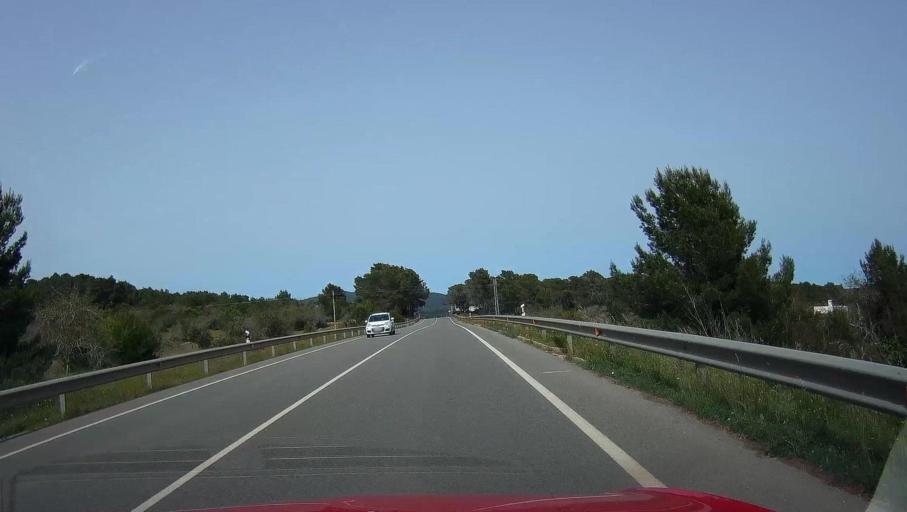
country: ES
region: Balearic Islands
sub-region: Illes Balears
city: Santa Eularia des Riu
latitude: 38.9971
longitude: 1.4889
